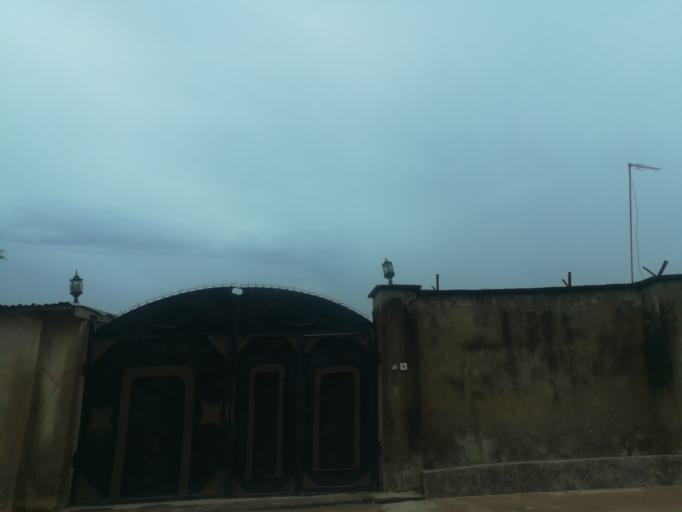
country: NG
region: Oyo
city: Ibadan
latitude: 7.3298
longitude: 3.8925
